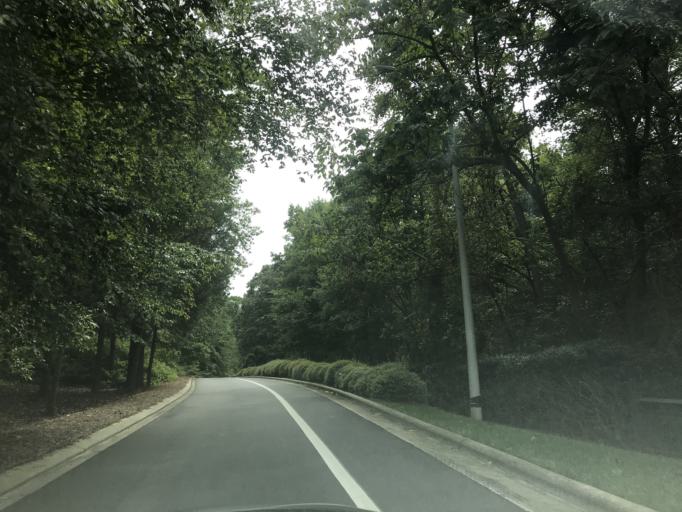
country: US
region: North Carolina
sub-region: Wake County
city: Cary
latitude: 35.7358
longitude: -78.7849
